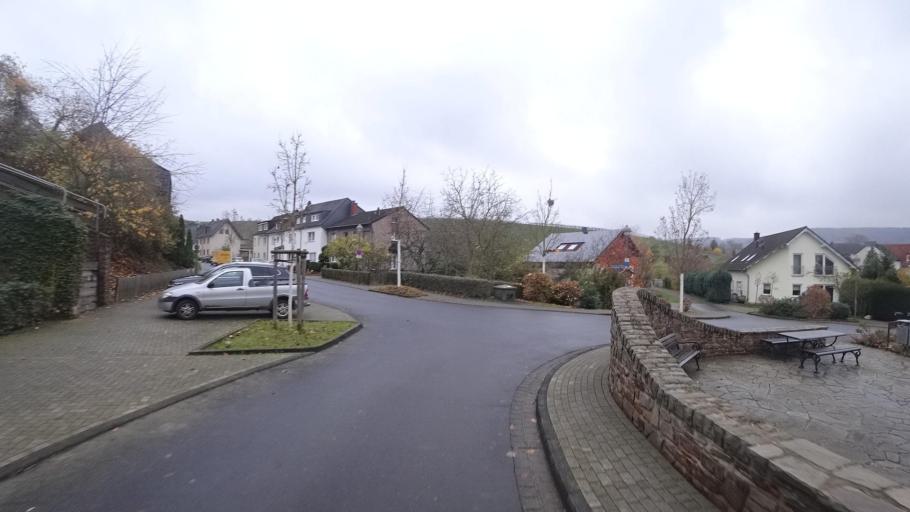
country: DE
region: Rheinland-Pfalz
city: Bad Neuenahr-Ahrweiler
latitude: 50.5382
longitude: 7.1124
